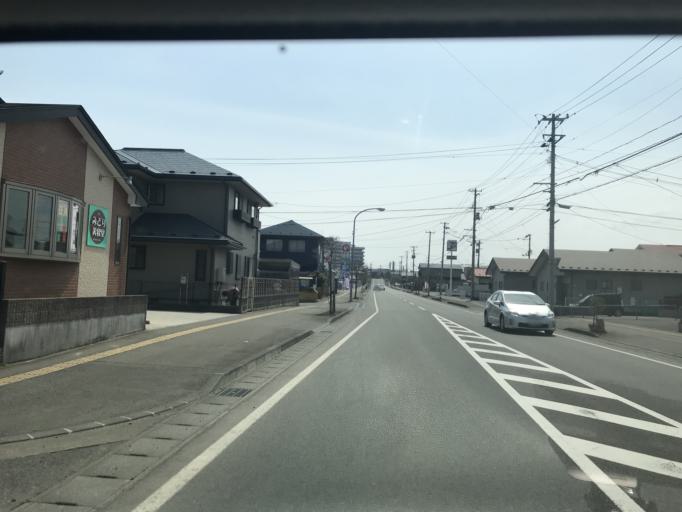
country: JP
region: Iwate
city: Mizusawa
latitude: 39.1281
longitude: 141.1357
